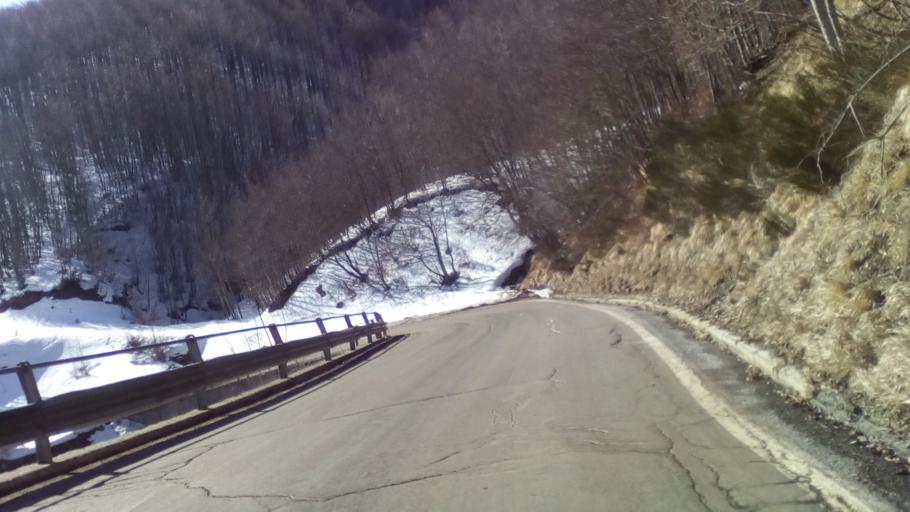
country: IT
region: Tuscany
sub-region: Provincia di Lucca
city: Fosciandora
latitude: 44.2047
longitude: 10.4941
